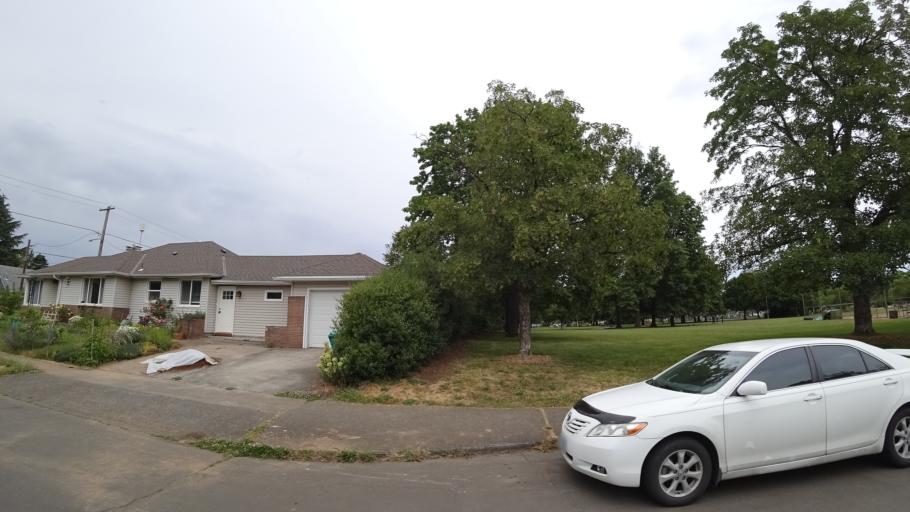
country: US
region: Oregon
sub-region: Multnomah County
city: Portland
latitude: 45.5717
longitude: -122.6950
